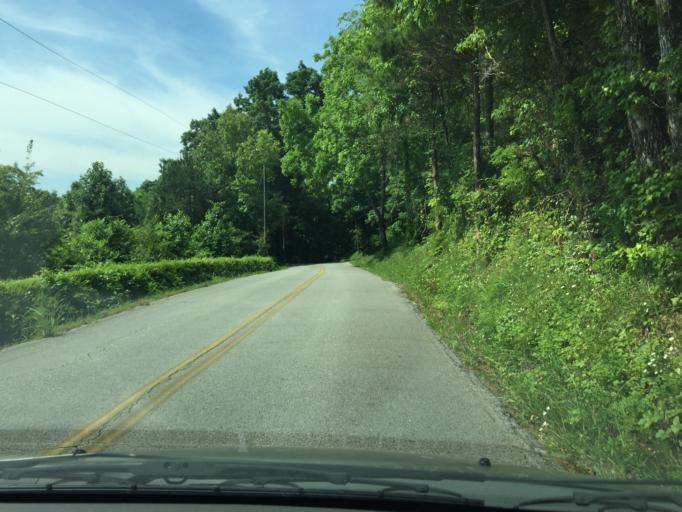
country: US
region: Tennessee
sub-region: Hamilton County
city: Collegedale
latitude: 35.0564
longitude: -85.0490
